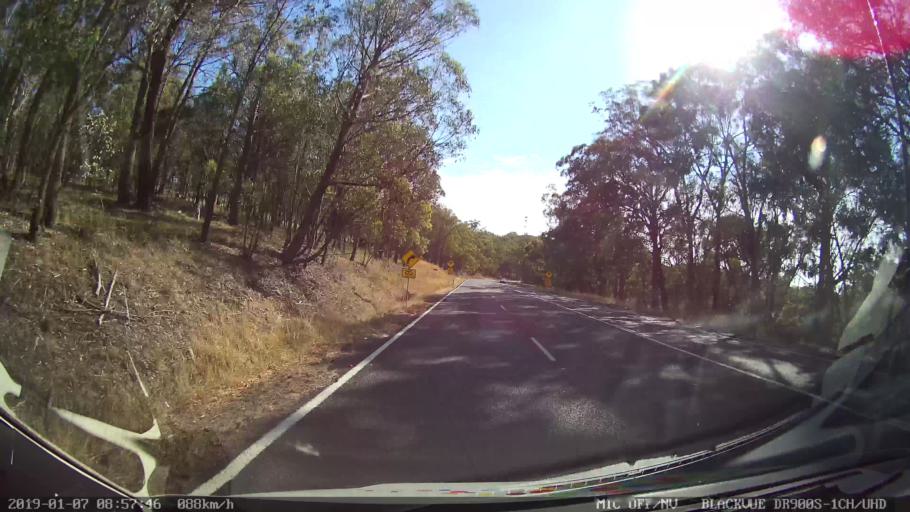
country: AU
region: New South Wales
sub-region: Armidale Dumaresq
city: Armidale
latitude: -30.7647
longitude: 151.3570
